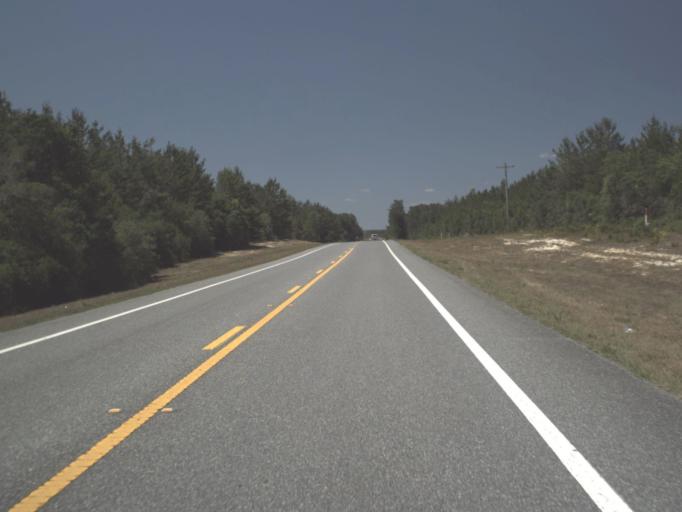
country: US
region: Florida
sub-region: Lake County
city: Astor
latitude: 29.1583
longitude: -81.6374
